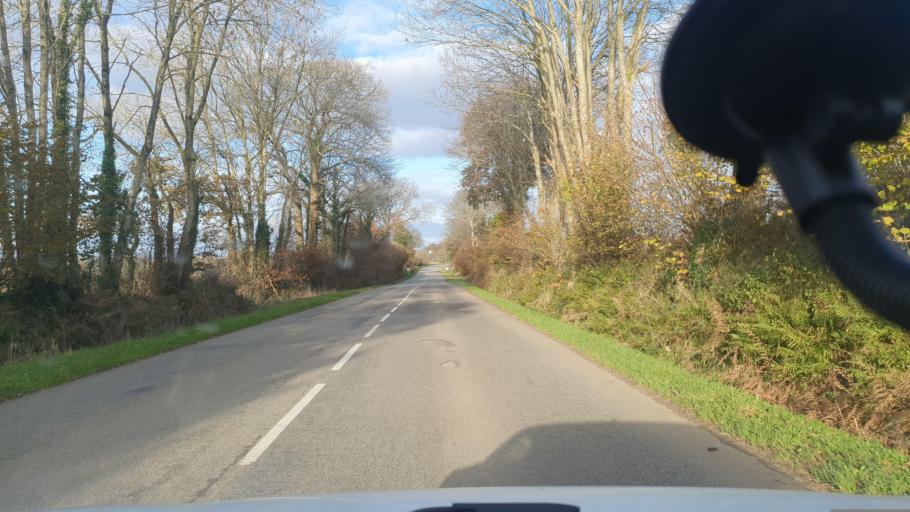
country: FR
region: Brittany
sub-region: Departement du Finistere
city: Briec
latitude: 48.0599
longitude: -4.0223
